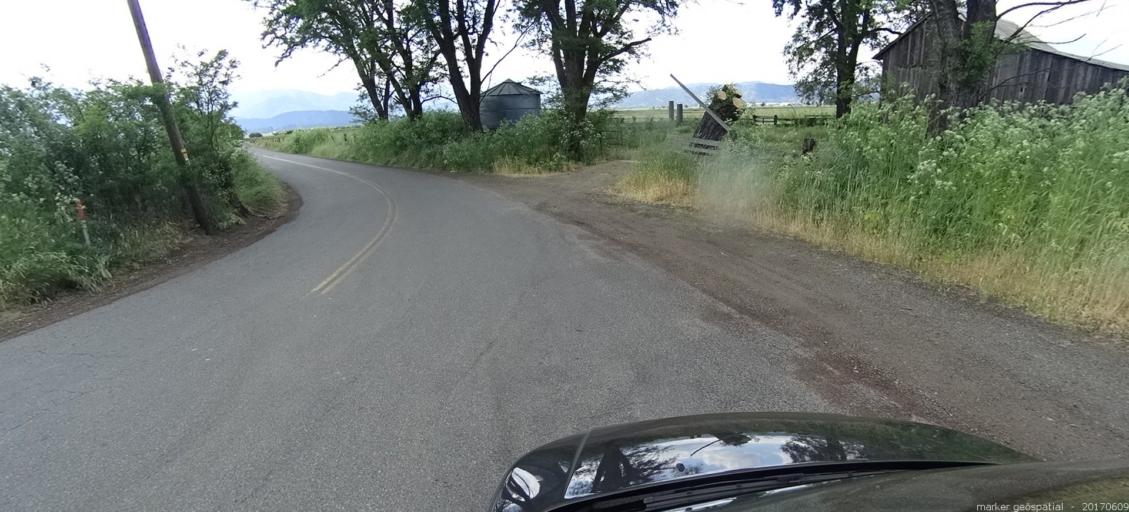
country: US
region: California
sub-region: Siskiyou County
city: Yreka
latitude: 41.5194
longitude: -122.8515
